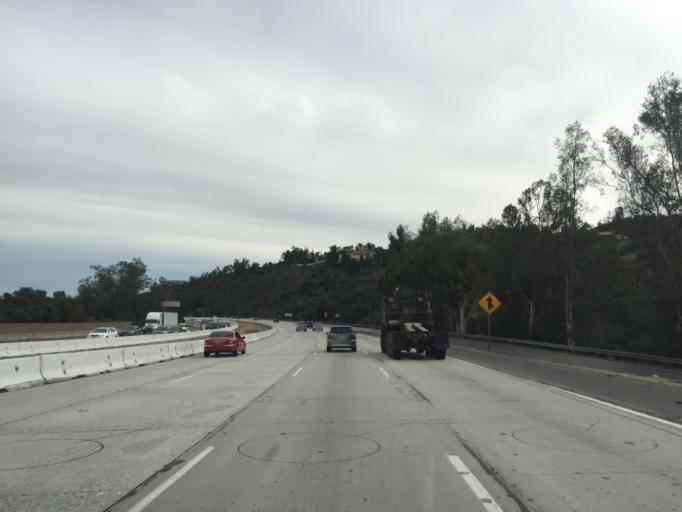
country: US
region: California
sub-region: Los Angeles County
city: La Canada Flintridge
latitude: 34.1896
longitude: -118.1810
